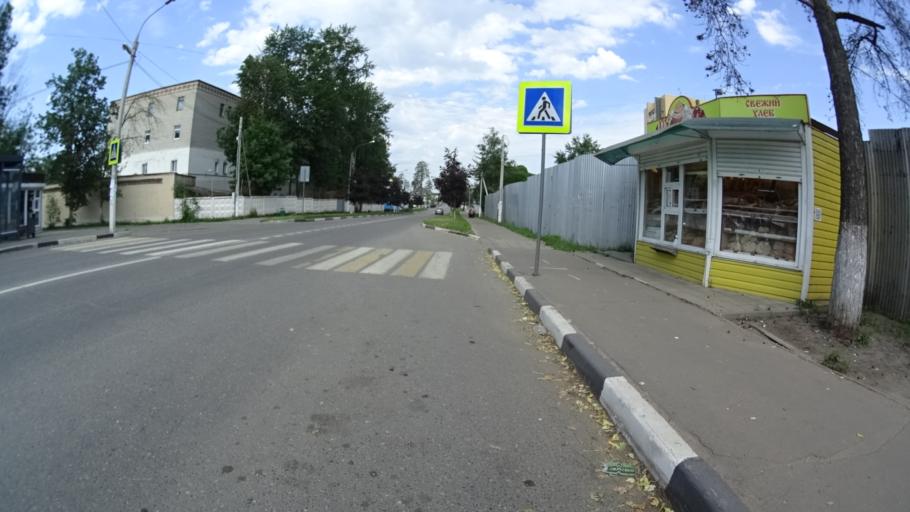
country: RU
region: Moskovskaya
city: Lesnoy
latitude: 56.0812
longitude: 37.9271
